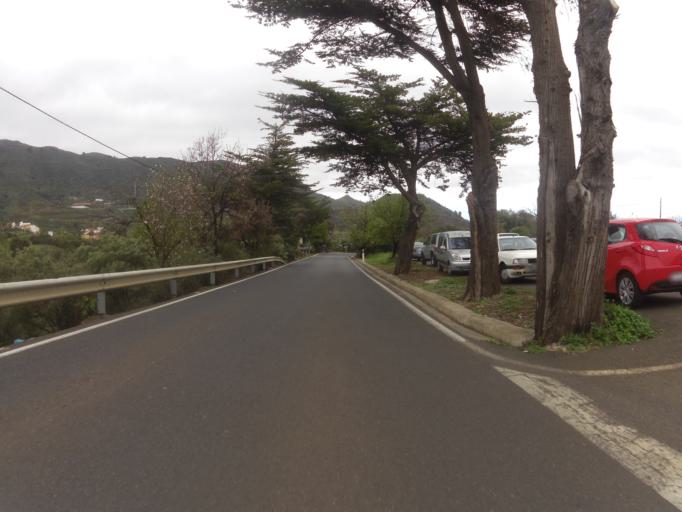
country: ES
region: Canary Islands
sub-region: Provincia de Las Palmas
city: Valsequillo de Gran Canaria
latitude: 27.9873
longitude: -15.5159
